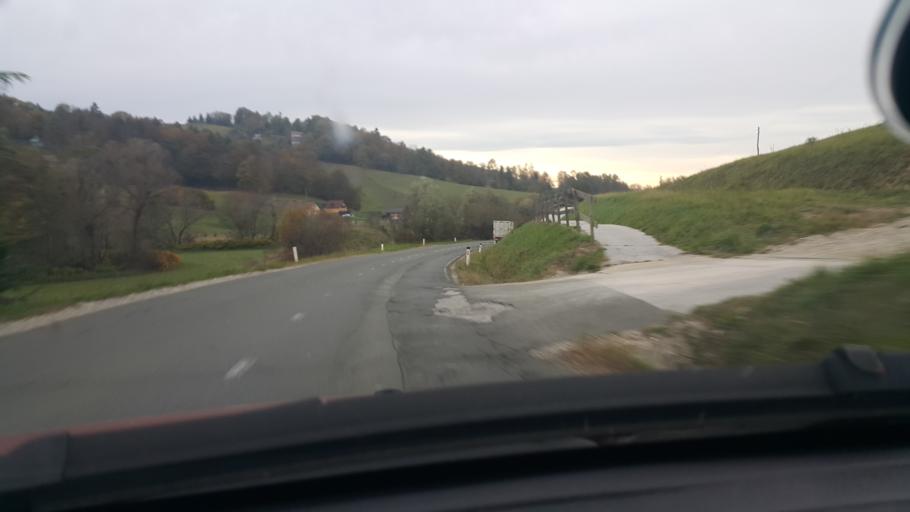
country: SI
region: Kungota
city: Zgornja Kungota
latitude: 46.6201
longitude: 15.6352
